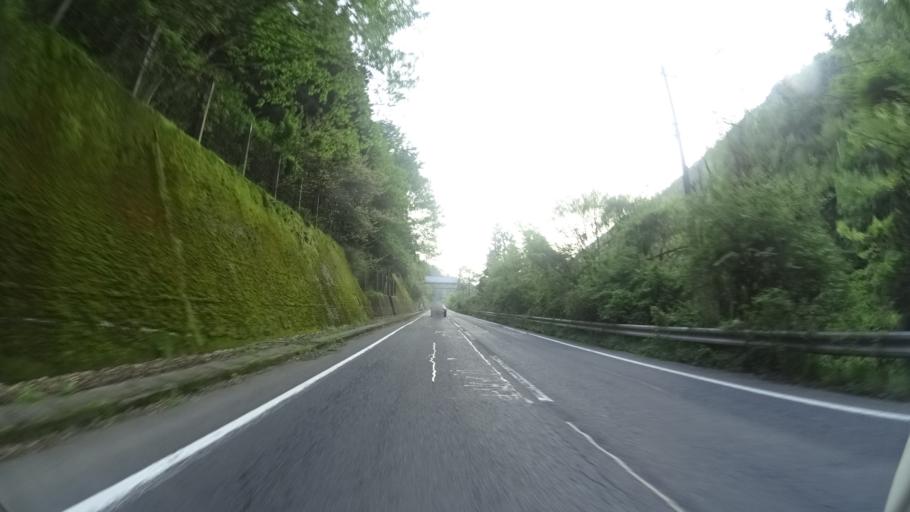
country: JP
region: Tokushima
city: Ikedacho
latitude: 34.0000
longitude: 133.6980
